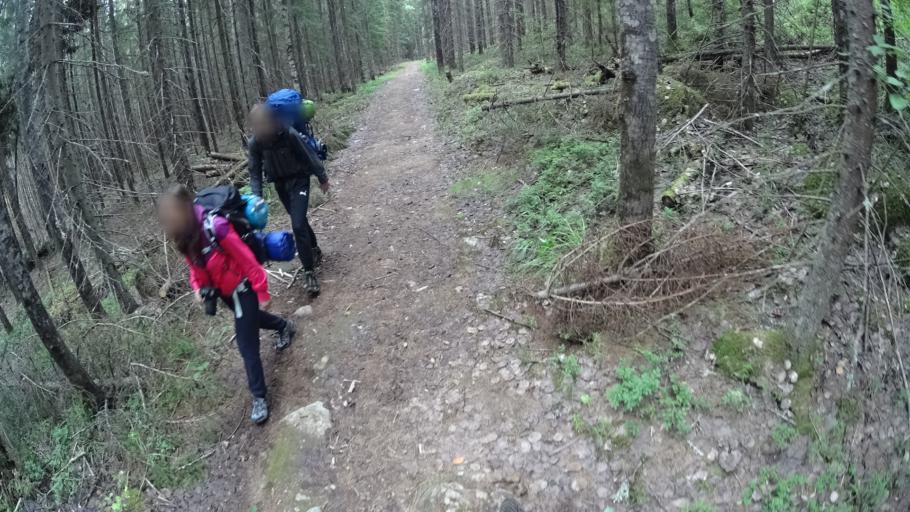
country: FI
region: Southern Savonia
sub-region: Mikkeli
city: Maentyharju
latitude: 61.1805
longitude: 26.8949
